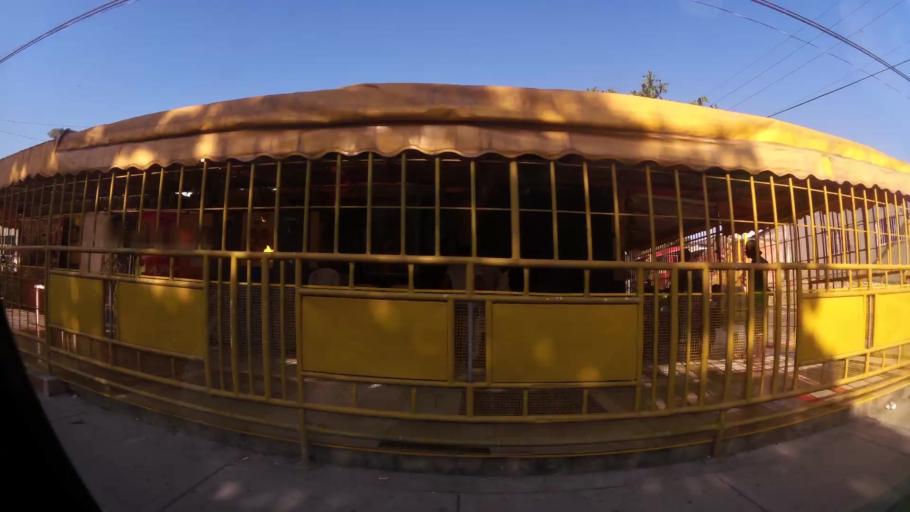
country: CO
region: Bolivar
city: Cartagena
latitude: 10.4018
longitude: -75.5003
